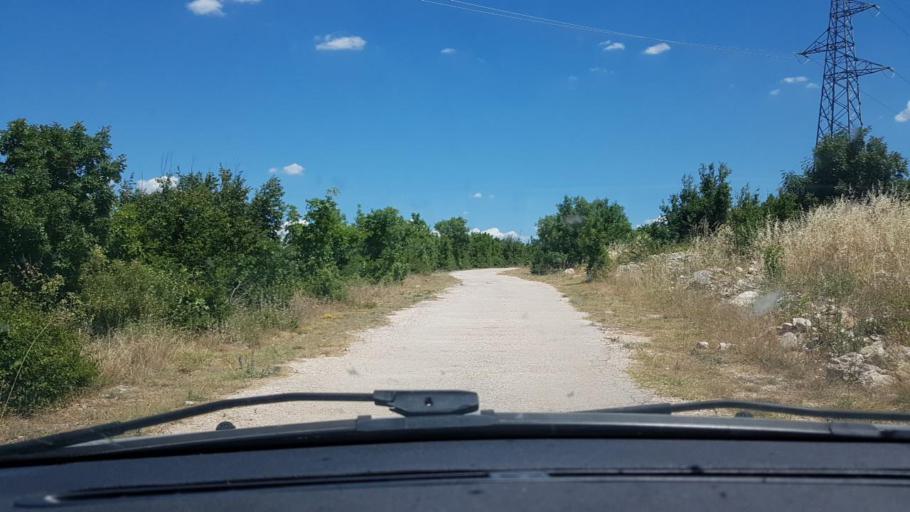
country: HR
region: Sibensko-Kniniska
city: Kistanje
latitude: 44.0020
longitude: 16.0248
